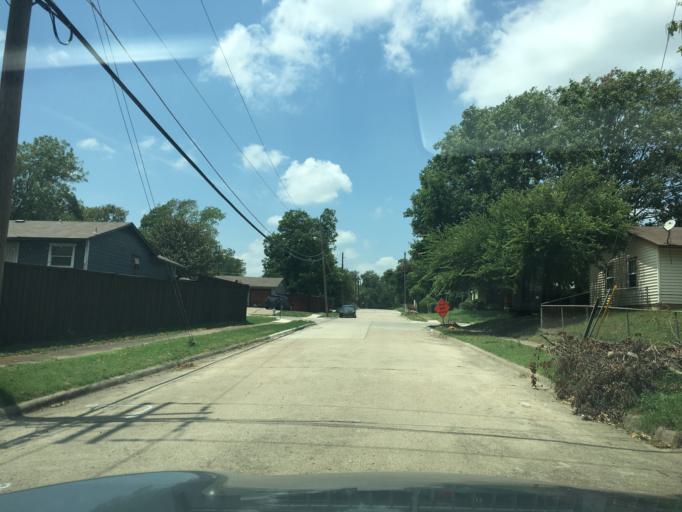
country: US
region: Texas
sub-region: Dallas County
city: Richardson
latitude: 32.9136
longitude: -96.7579
